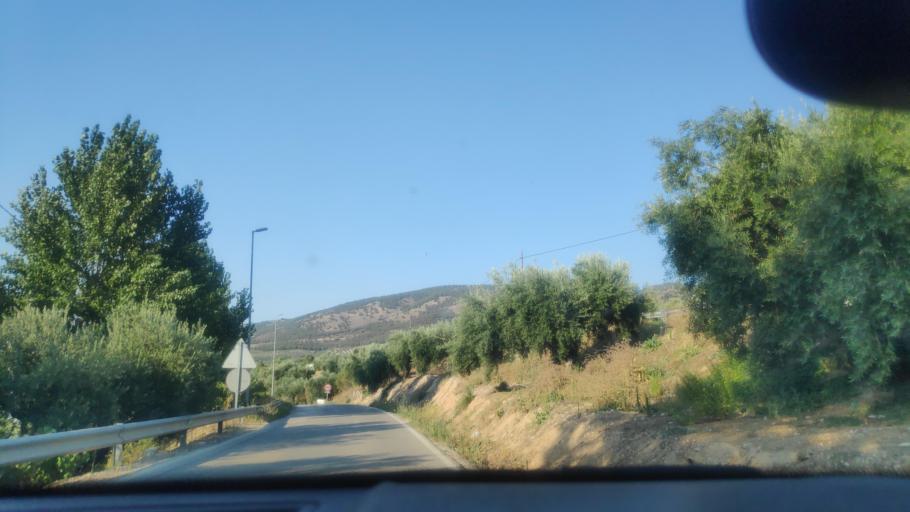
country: ES
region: Andalusia
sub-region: Provincia de Jaen
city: Jaen
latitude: 37.7225
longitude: -3.7600
